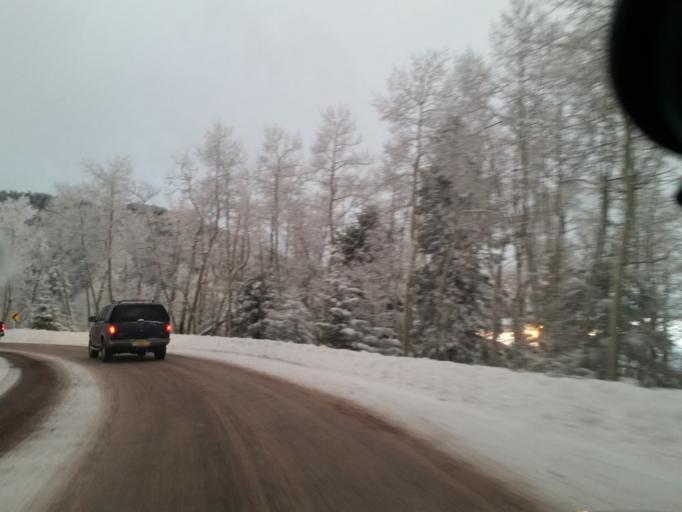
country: US
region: New Mexico
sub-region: Santa Fe County
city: Santa Fe
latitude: 35.7647
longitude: -105.8128
